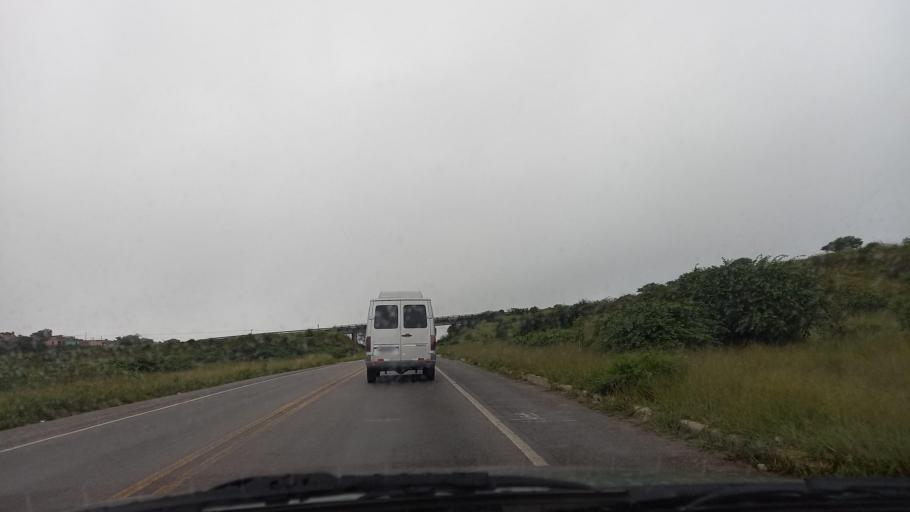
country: BR
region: Pernambuco
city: Garanhuns
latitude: -8.8746
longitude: -36.5076
